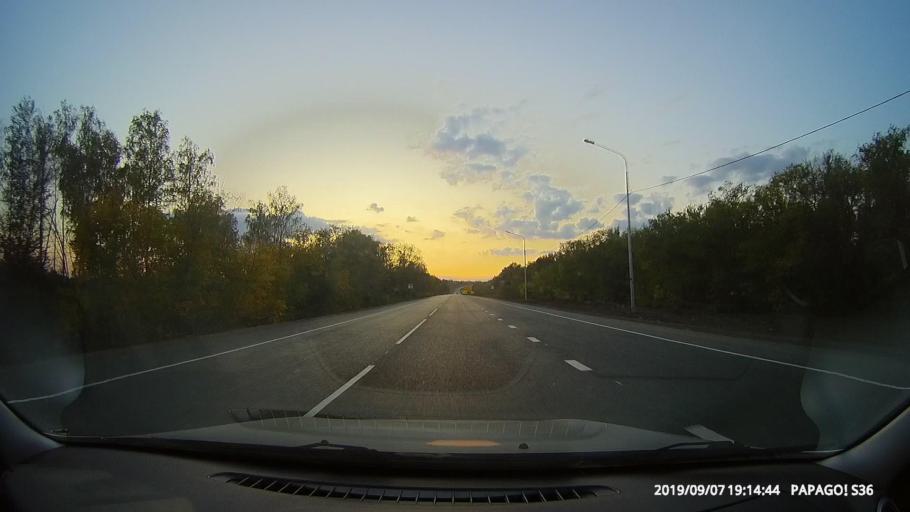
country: RU
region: Samara
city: Chapayevsk
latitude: 52.9972
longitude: 49.7693
